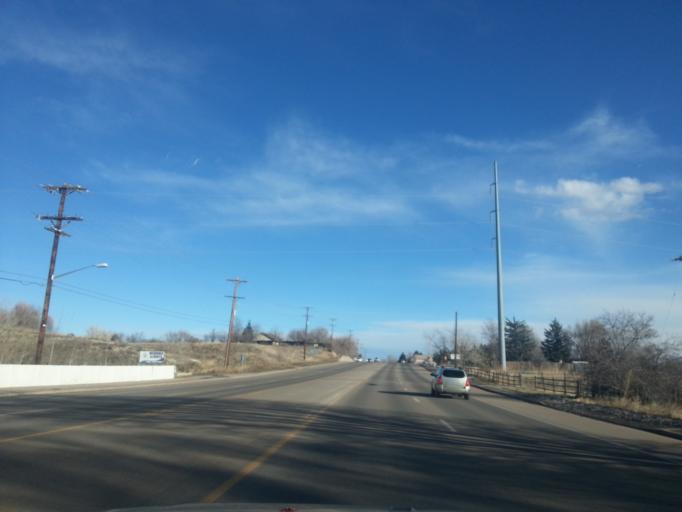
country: US
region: Colorado
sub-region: Larimer County
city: Loveland
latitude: 40.4073
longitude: -105.1296
